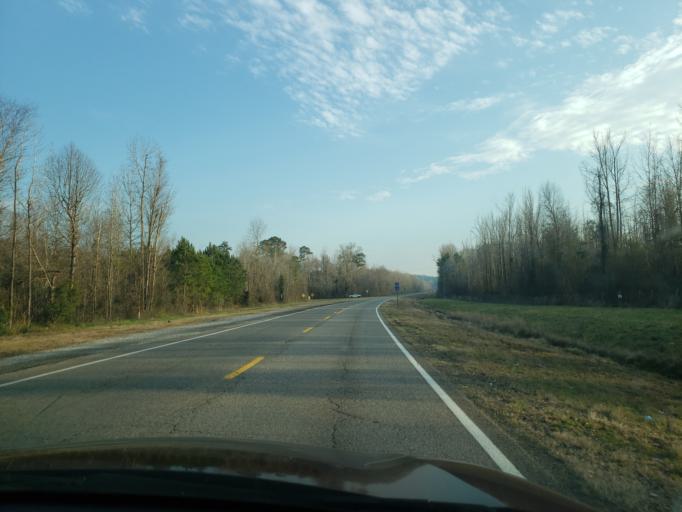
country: US
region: Alabama
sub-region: Hale County
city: Greensboro
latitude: 32.7744
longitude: -87.5858
